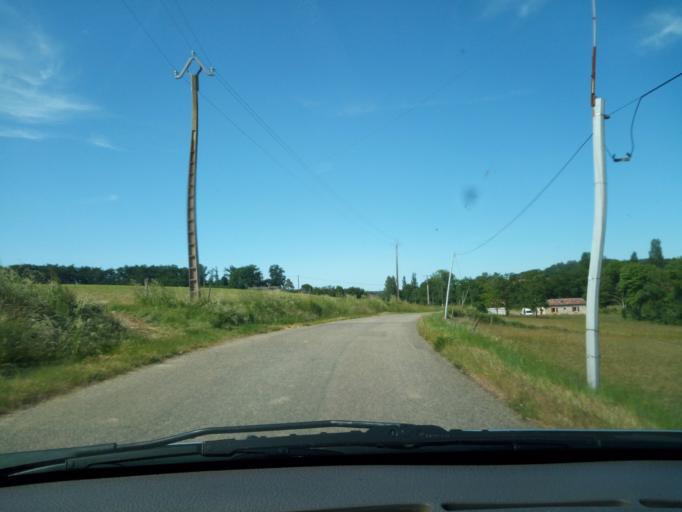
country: FR
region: Midi-Pyrenees
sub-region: Departement du Tarn-et-Garonne
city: Molieres
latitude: 44.2210
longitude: 1.3263
